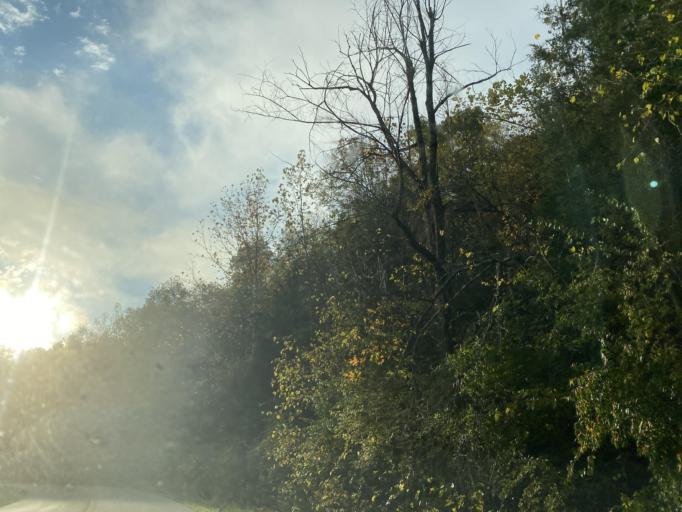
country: US
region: Kentucky
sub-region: Pendleton County
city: Falmouth
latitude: 38.7188
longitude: -84.2994
